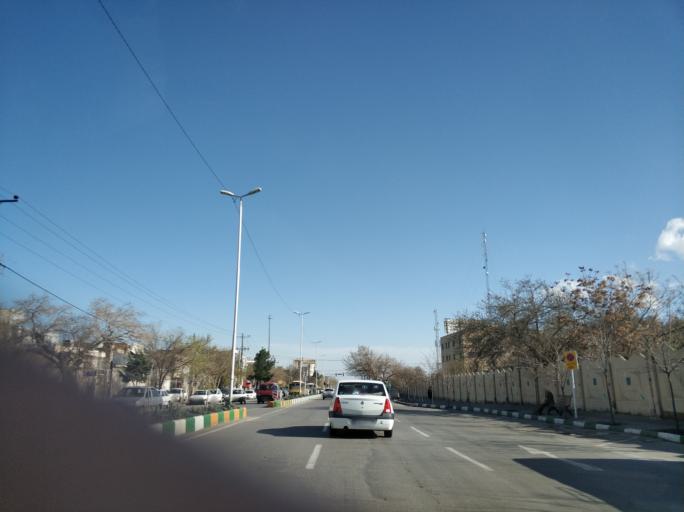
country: IR
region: Razavi Khorasan
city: Mashhad
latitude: 36.3005
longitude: 59.6325
